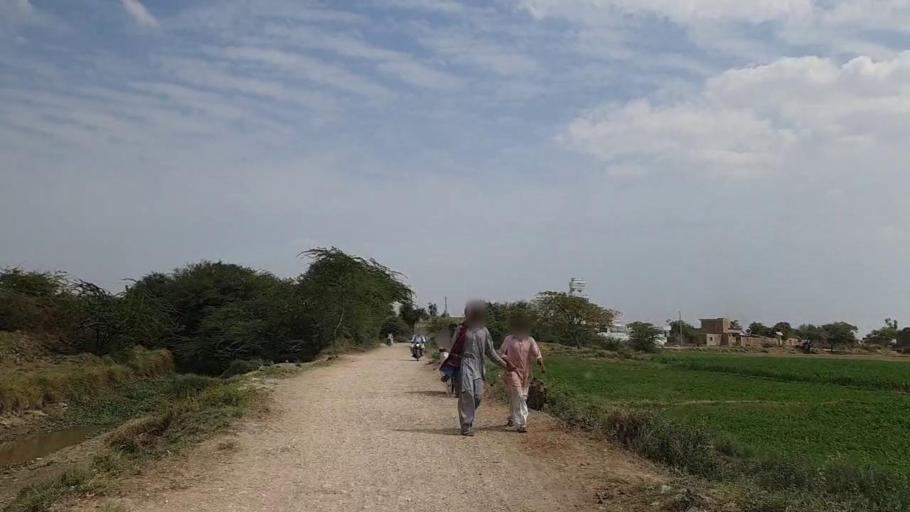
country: PK
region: Sindh
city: Daro Mehar
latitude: 24.8437
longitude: 68.1932
